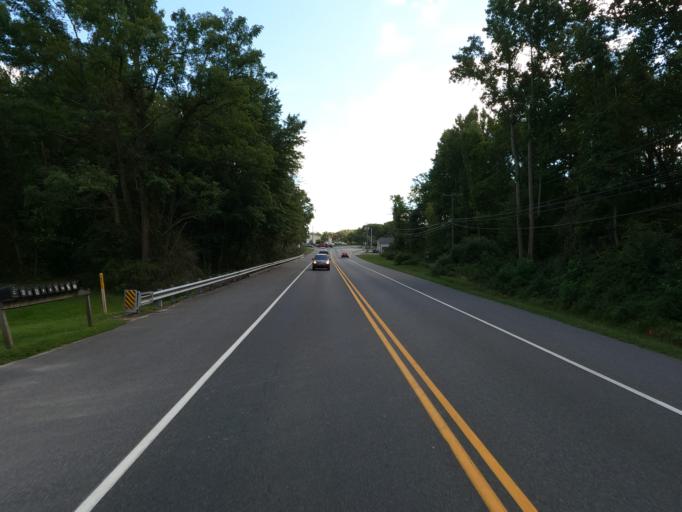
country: US
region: Delaware
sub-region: New Castle County
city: Glasgow
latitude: 39.6069
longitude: -75.7695
